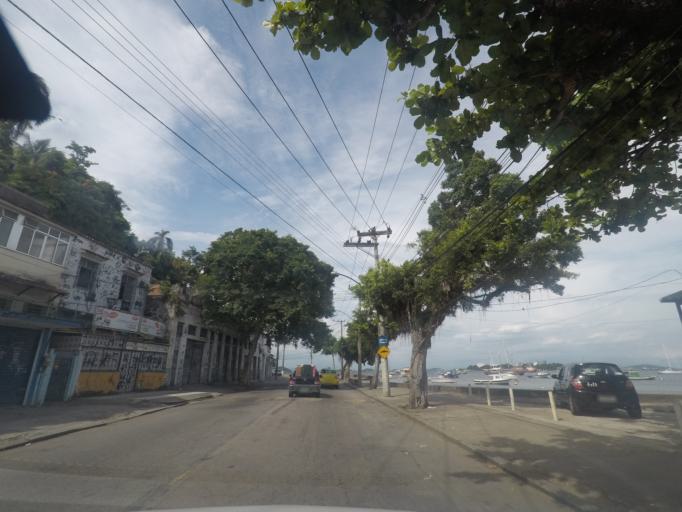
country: BR
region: Rio de Janeiro
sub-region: Rio De Janeiro
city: Rio de Janeiro
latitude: -22.8192
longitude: -43.1756
